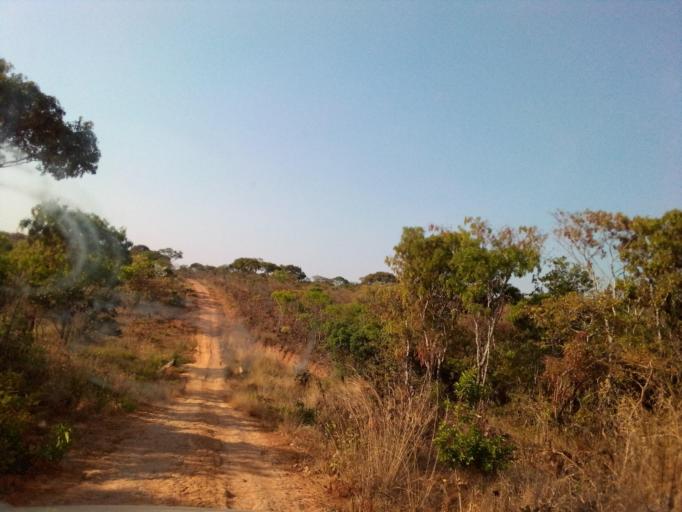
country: ZM
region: Northern
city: Mpika
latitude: -12.2118
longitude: 31.4365
